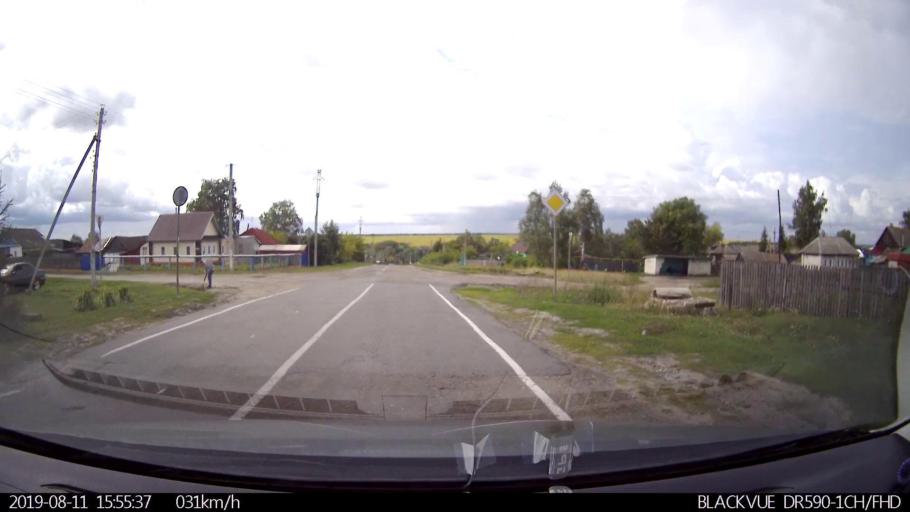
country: RU
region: Ulyanovsk
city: Ignatovka
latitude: 53.9458
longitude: 47.6533
